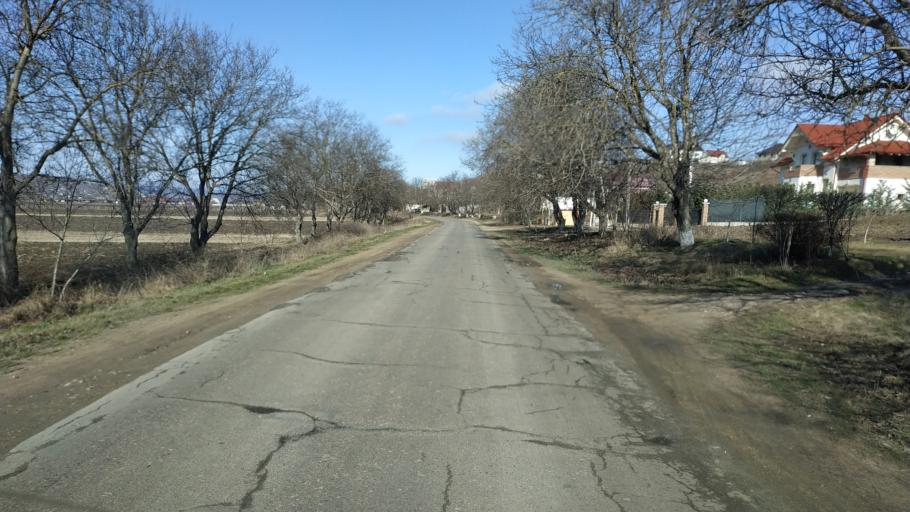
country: MD
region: Laloveni
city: Ialoveni
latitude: 46.9293
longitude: 28.6714
